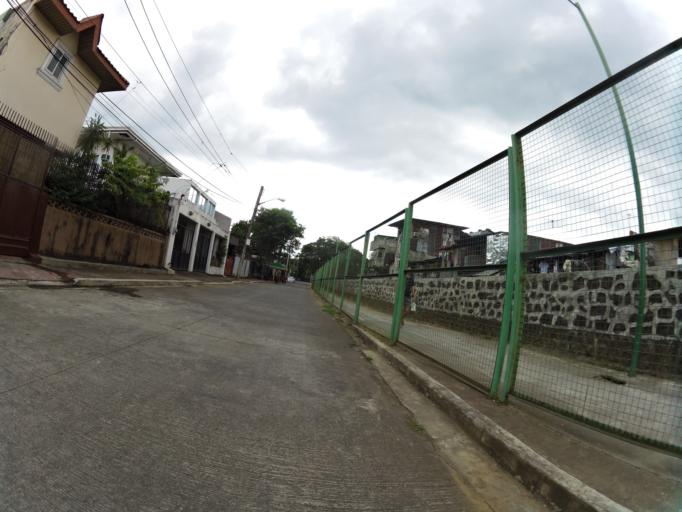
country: PH
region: Calabarzon
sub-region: Province of Rizal
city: Antipolo
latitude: 14.6365
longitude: 121.1094
